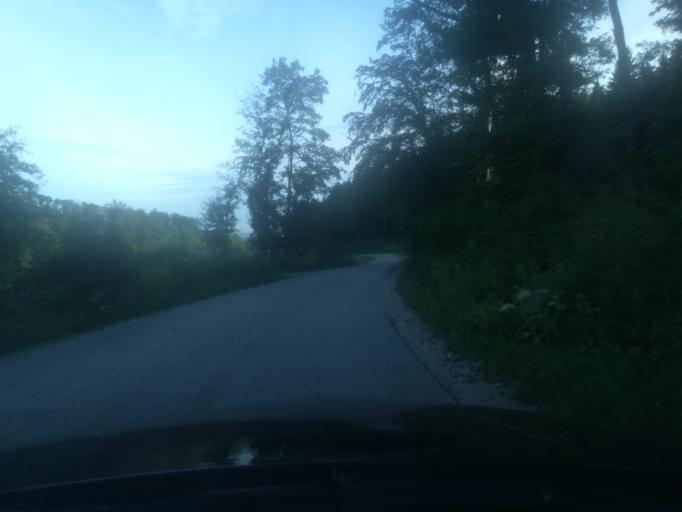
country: AT
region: Upper Austria
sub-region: Wels-Land
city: Marchtrenk
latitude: 48.1701
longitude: 14.1649
